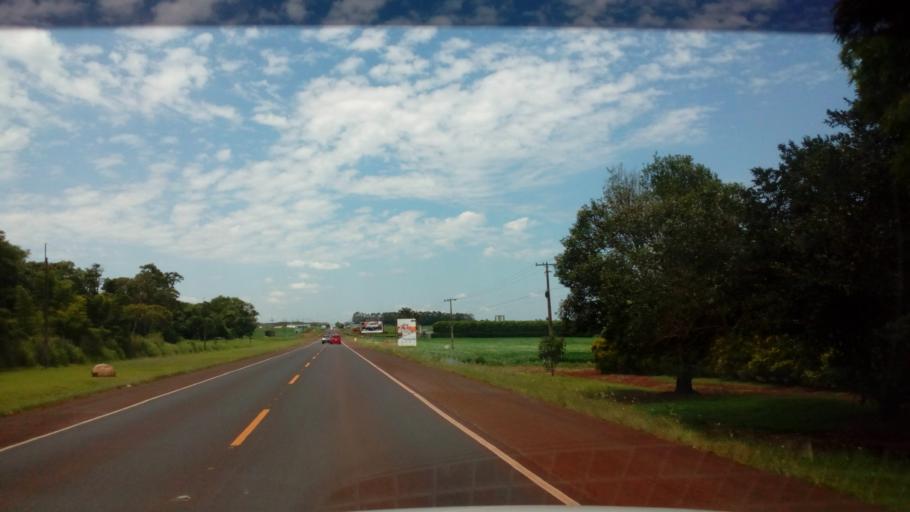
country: PY
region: Alto Parana
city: Santa Rita
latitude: -25.7373
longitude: -55.0467
